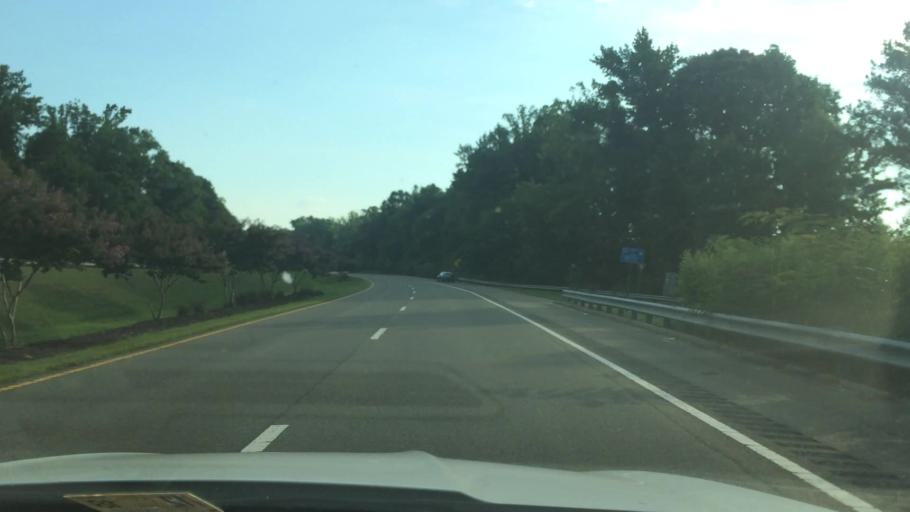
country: US
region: Virginia
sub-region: City of Williamsburg
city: Williamsburg
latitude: 37.2586
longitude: -76.6436
